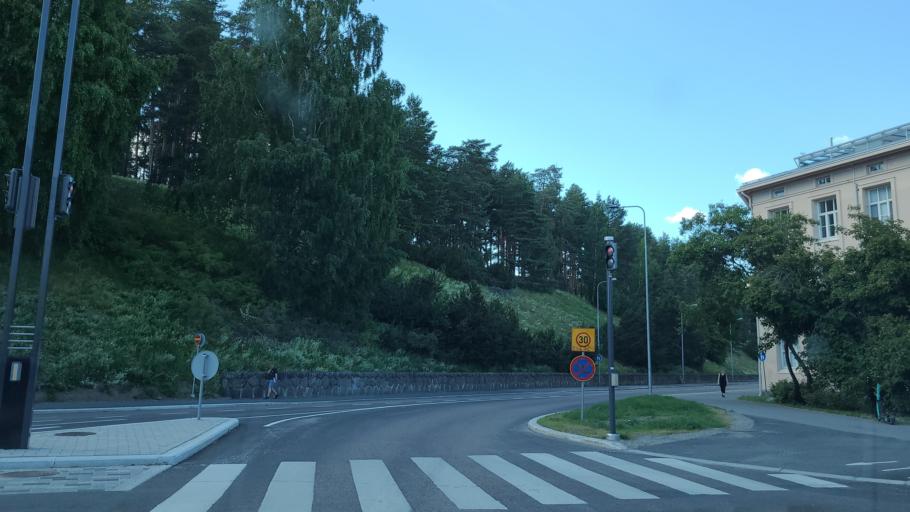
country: FI
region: Central Finland
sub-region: Jyvaeskylae
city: Jyvaeskylae
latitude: 62.2426
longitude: 25.7428
